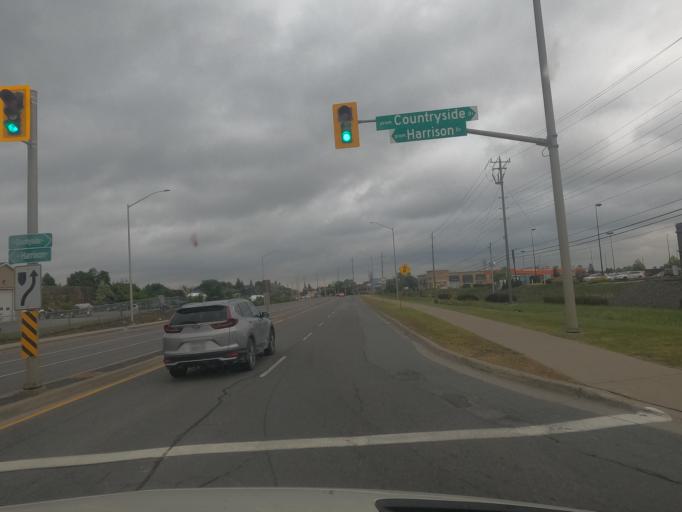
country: CA
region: Ontario
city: Greater Sudbury
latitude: 46.4396
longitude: -81.0056
